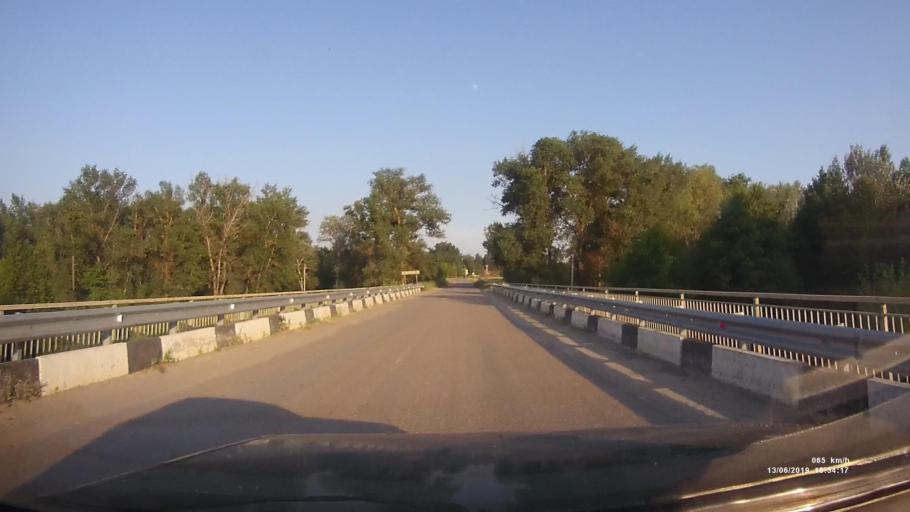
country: RU
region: Rostov
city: Kazanskaya
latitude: 49.8686
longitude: 41.3944
